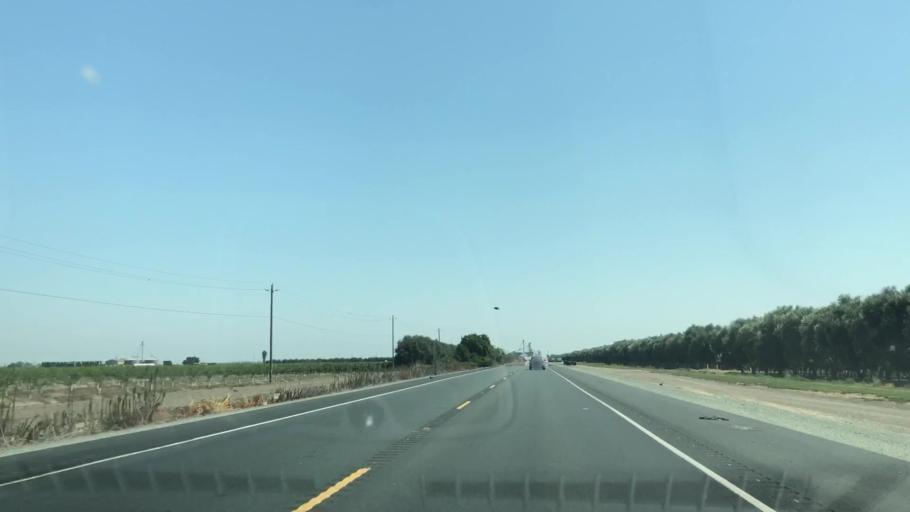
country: US
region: California
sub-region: San Joaquin County
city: Thornton
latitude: 38.1154
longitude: -121.4413
